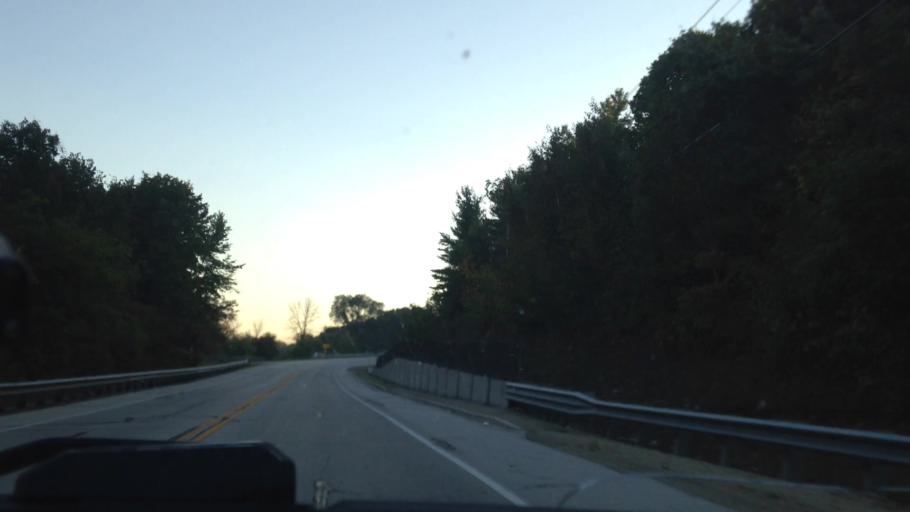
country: US
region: Wisconsin
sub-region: Washington County
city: Newburg
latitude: 43.4251
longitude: -88.0598
